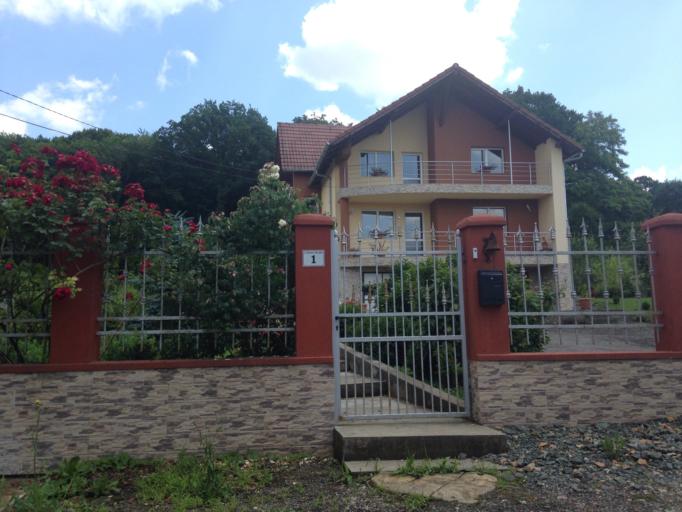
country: RO
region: Cluj
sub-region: Comuna Feleacu
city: Feleacu
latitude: 46.7256
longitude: 23.5810
